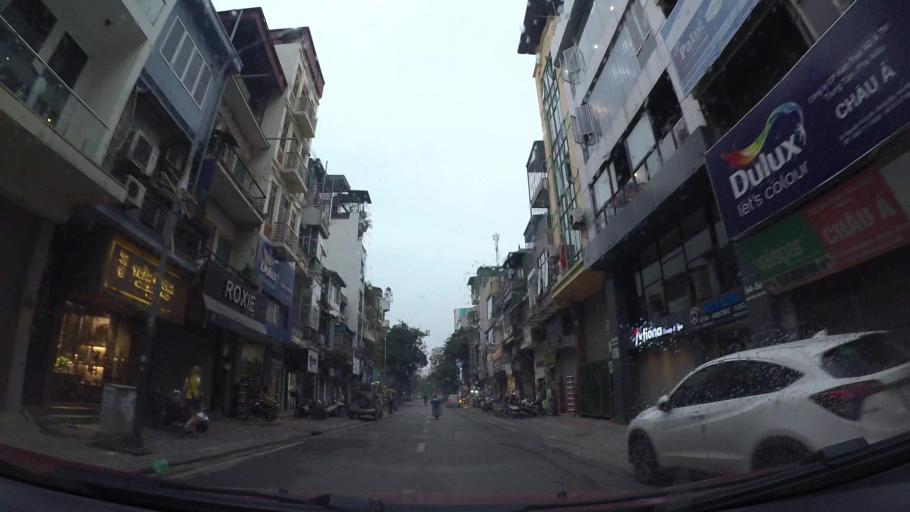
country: VN
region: Ha Noi
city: Hanoi
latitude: 21.0280
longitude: 105.8399
